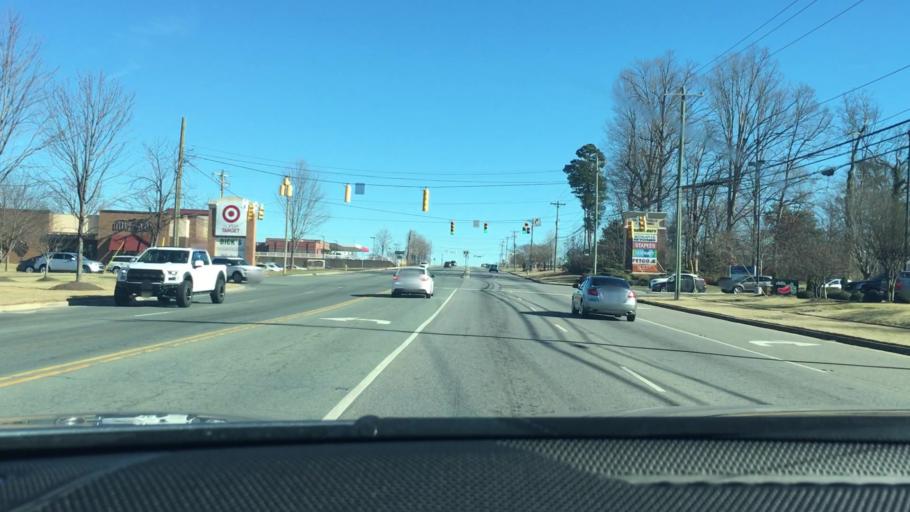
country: US
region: North Carolina
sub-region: Iredell County
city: Mooresville
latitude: 35.5956
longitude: -80.8729
